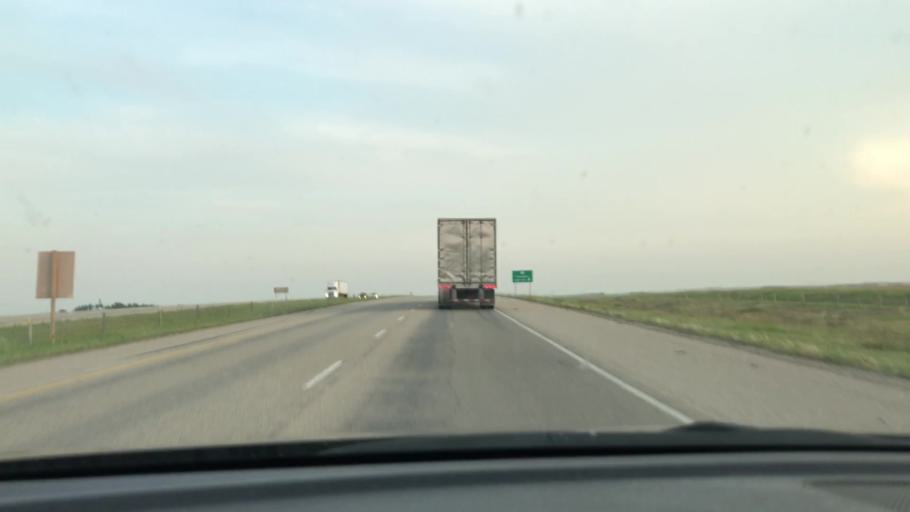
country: CA
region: Alberta
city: Carstairs
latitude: 51.5741
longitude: -114.0255
